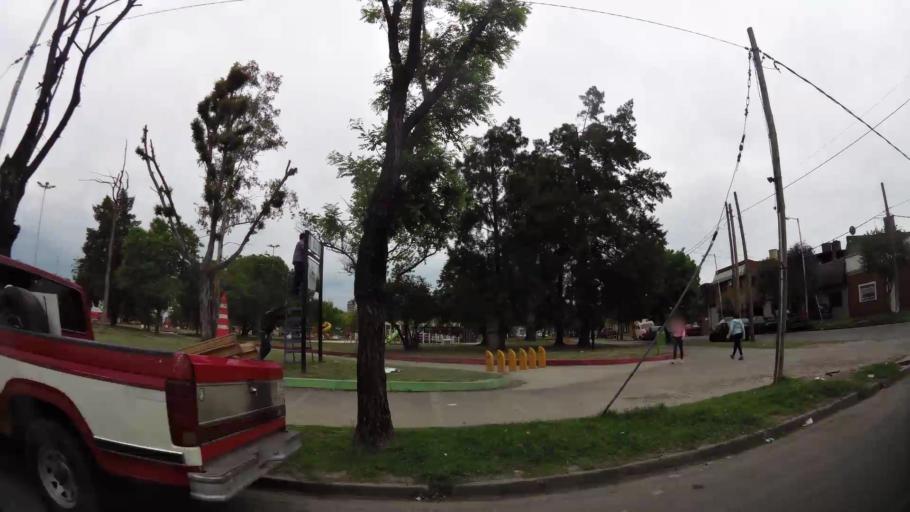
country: AR
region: Buenos Aires
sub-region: Partido de Avellaneda
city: Avellaneda
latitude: -34.6652
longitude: -58.3495
